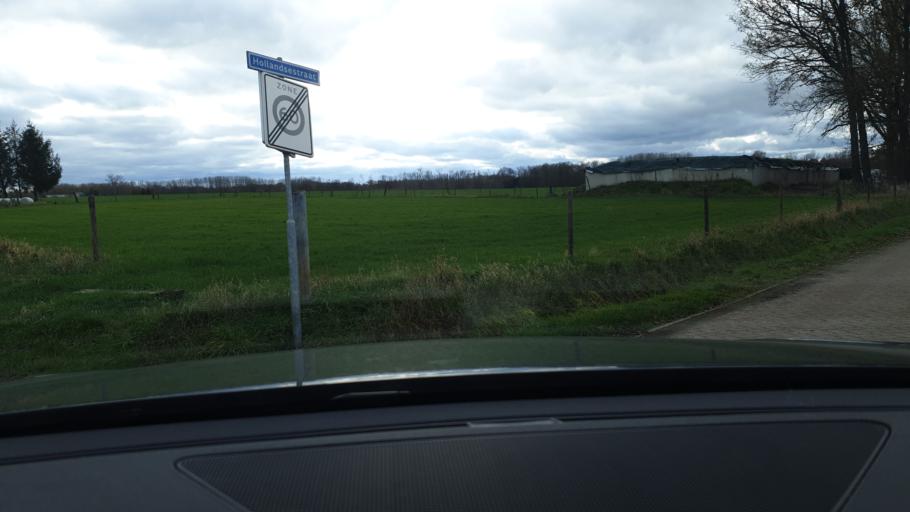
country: NL
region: North Brabant
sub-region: Gemeente Waalre
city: Waalre
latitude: 51.3790
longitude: 5.4334
